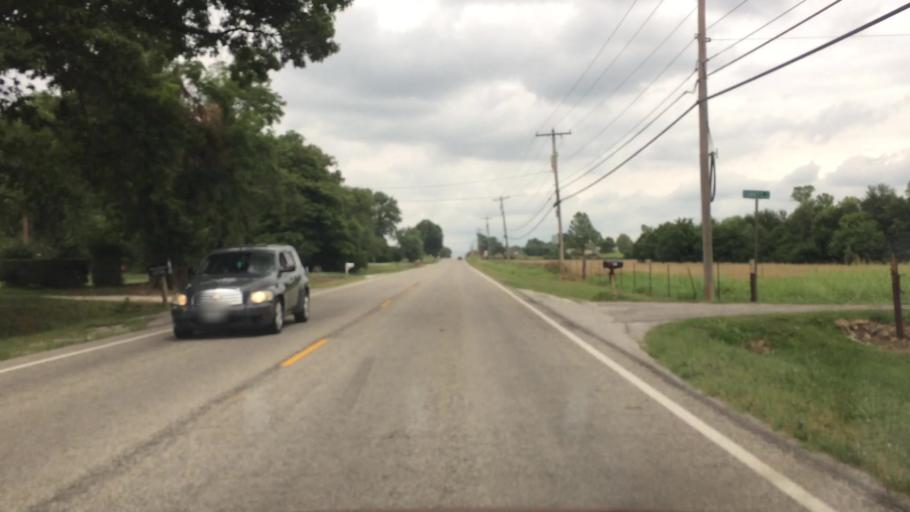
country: US
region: Missouri
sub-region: Greene County
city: Springfield
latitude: 37.2887
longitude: -93.2639
